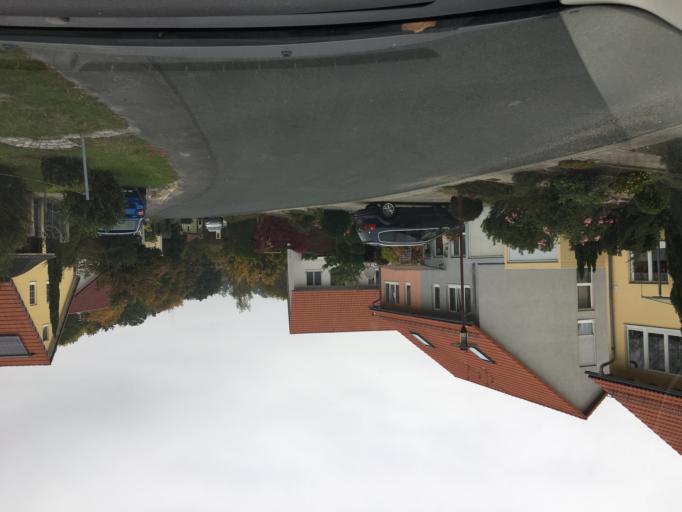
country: DE
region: Saxony
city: Freital
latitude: 51.0014
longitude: 13.6693
